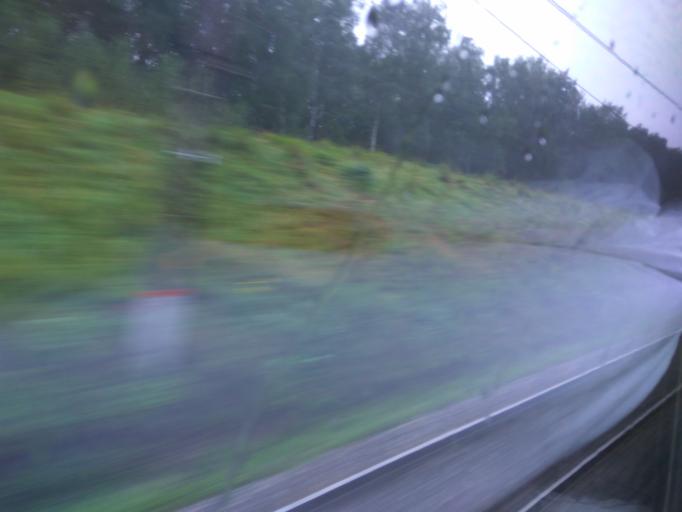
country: RU
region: Moskovskaya
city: Ozherel'ye
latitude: 54.8260
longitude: 38.2523
